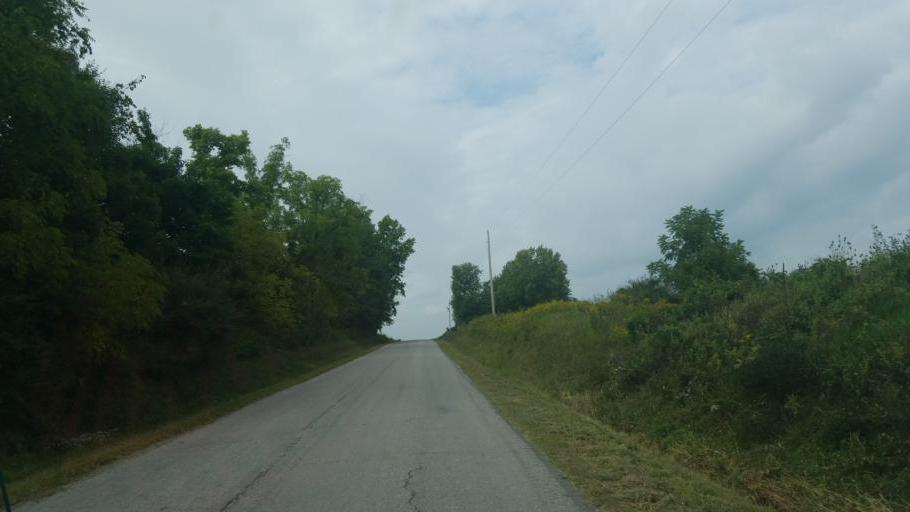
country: US
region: Ohio
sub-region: Wayne County
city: West Salem
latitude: 40.9621
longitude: -82.0538
